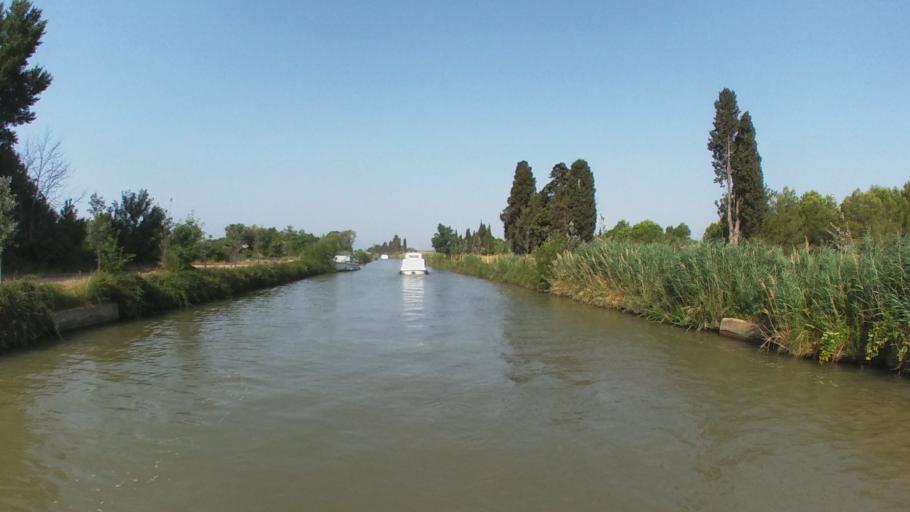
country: FR
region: Languedoc-Roussillon
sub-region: Departement de l'Herault
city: Olonzac
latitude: 43.2667
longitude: 2.7044
